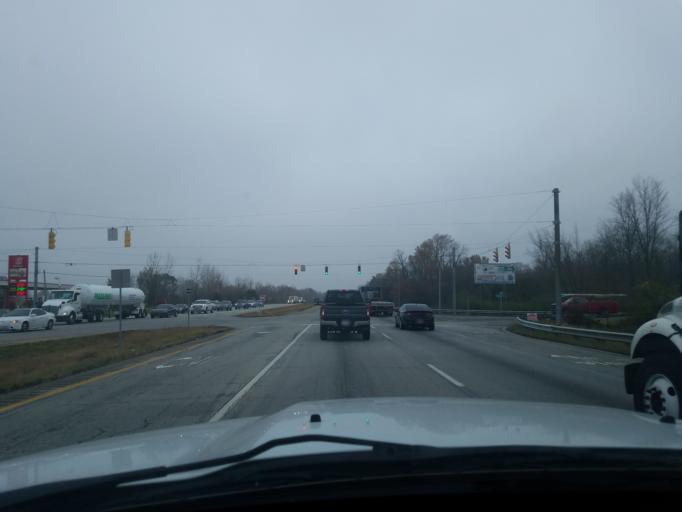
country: US
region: Indiana
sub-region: Hamilton County
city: Westfield
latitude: 40.1307
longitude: -86.1280
